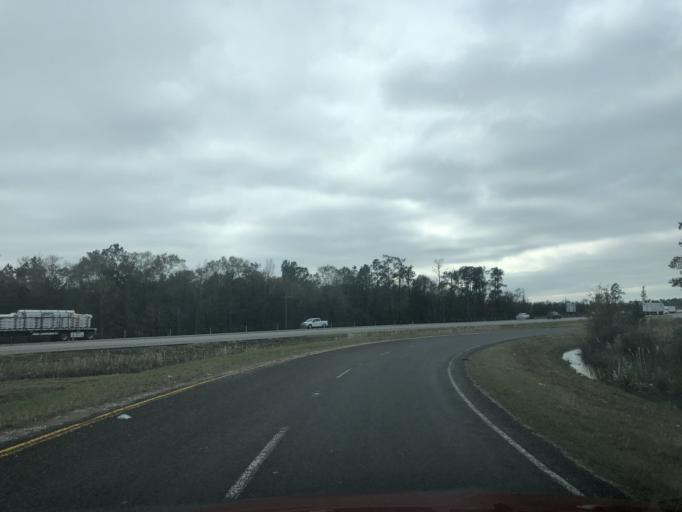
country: US
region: Texas
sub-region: Jefferson County
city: Fannett
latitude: 29.9300
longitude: -94.2718
